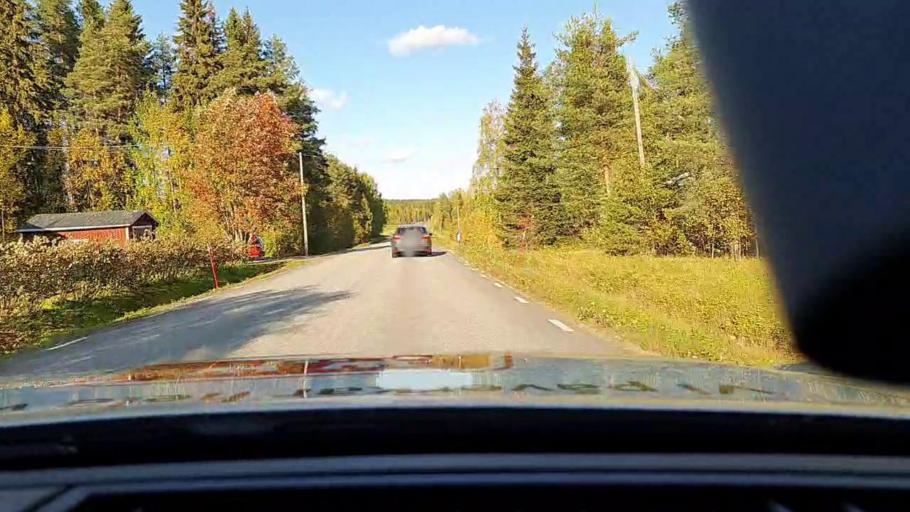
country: SE
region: Norrbotten
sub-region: Pitea Kommun
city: Norrfjarden
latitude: 65.5090
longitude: 21.4866
